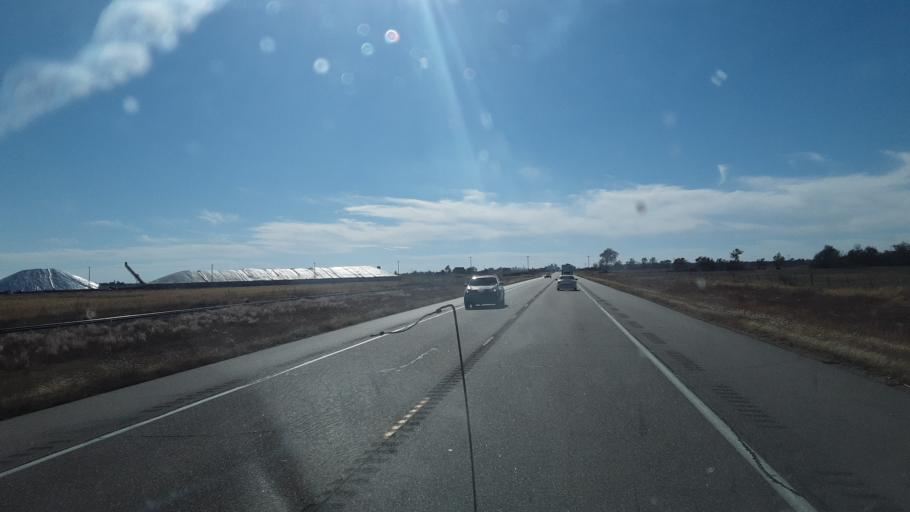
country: US
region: Kansas
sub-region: Pawnee County
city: Larned
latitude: 38.2063
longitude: -99.0624
